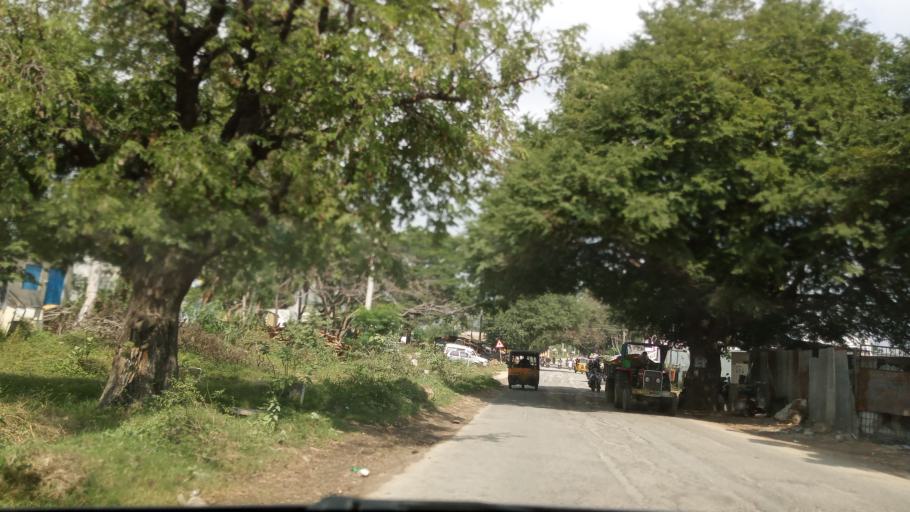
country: IN
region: Andhra Pradesh
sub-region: Chittoor
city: Madanapalle
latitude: 13.5707
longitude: 78.5160
